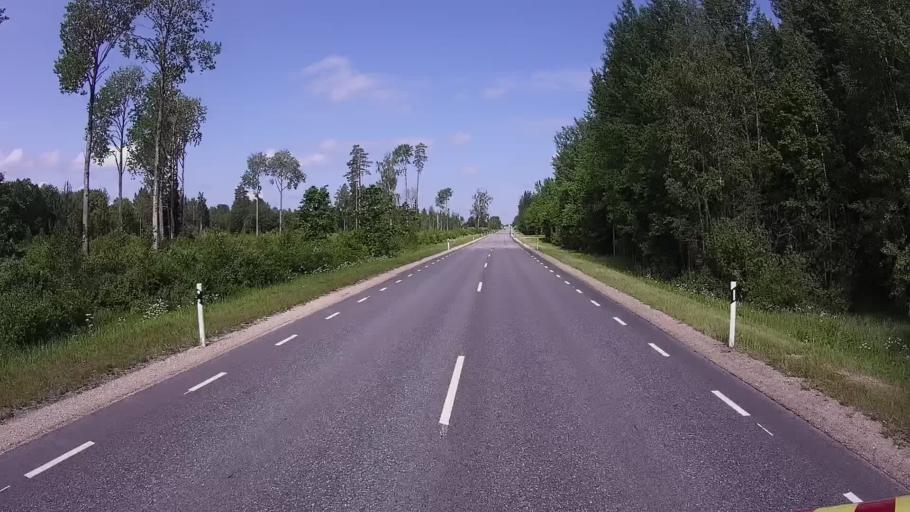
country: EE
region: Polvamaa
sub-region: Polva linn
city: Polva
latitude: 58.1678
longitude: 26.9162
